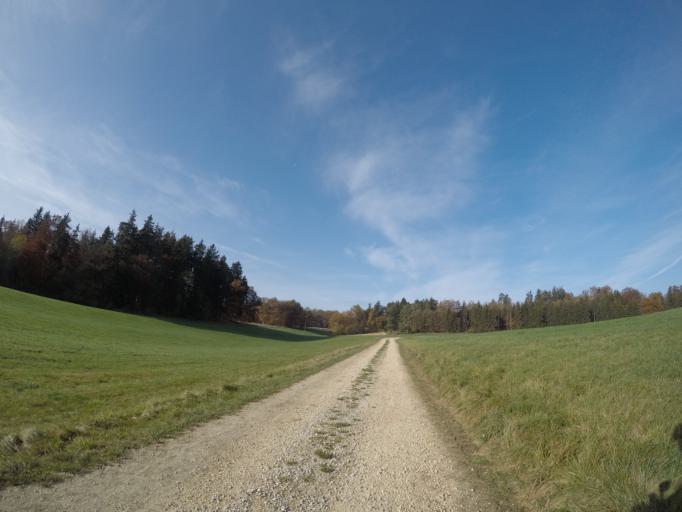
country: DE
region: Baden-Wuerttemberg
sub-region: Tuebingen Region
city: Bernstadt
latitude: 48.5122
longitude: 10.0185
